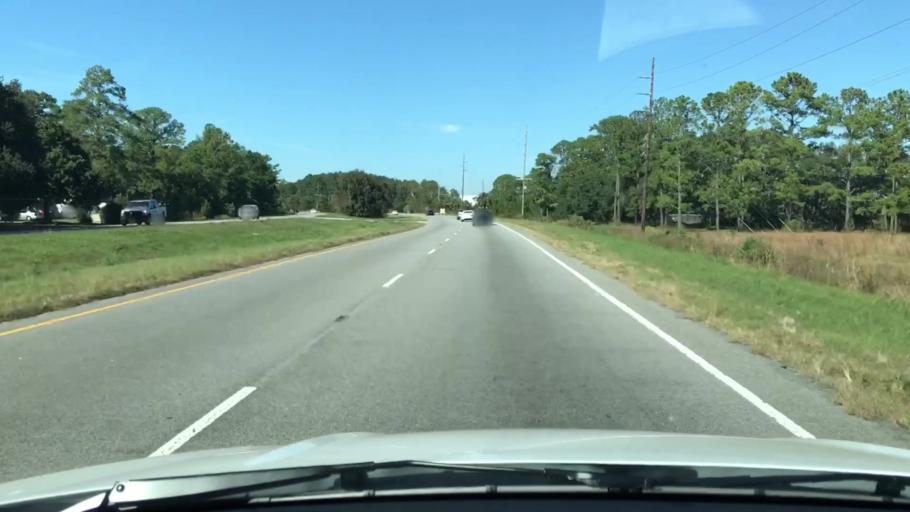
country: US
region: South Carolina
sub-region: Beaufort County
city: Laurel Bay
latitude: 32.5042
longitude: -80.7447
